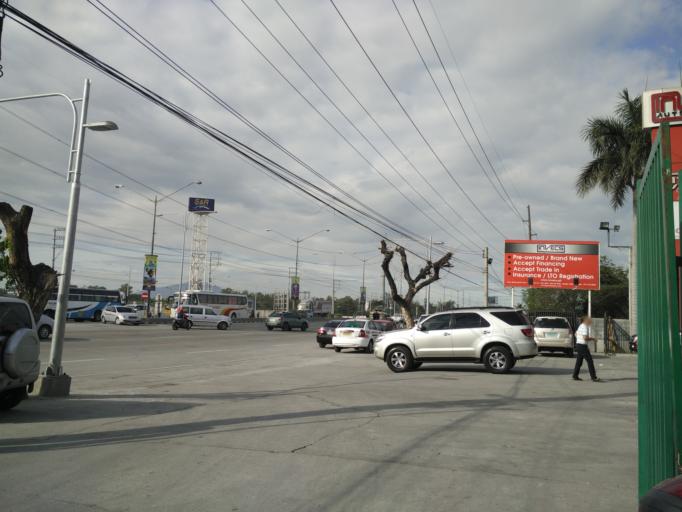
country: PH
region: Central Luzon
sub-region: Province of Pampanga
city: Del Pilar
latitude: 15.0460
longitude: 120.6912
